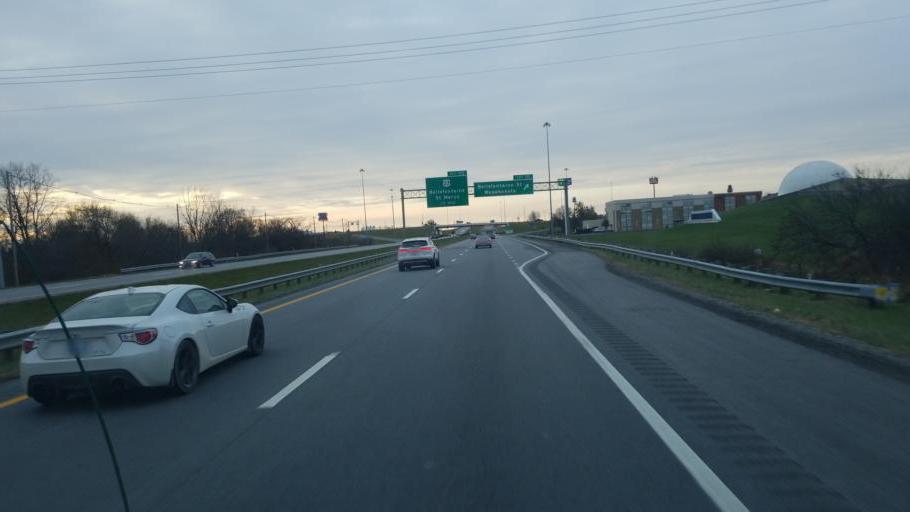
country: US
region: Ohio
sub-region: Auglaize County
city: Wapakoneta
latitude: 40.5655
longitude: -84.1702
